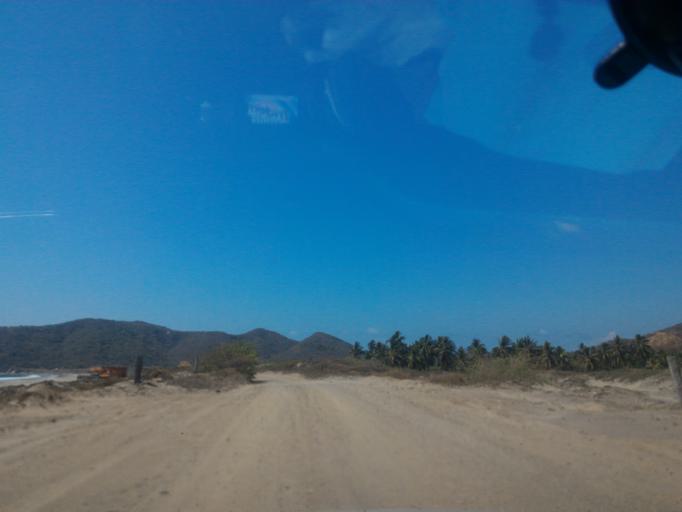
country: MX
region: Michoacan
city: Coahuayana Viejo
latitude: 18.5909
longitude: -103.6873
